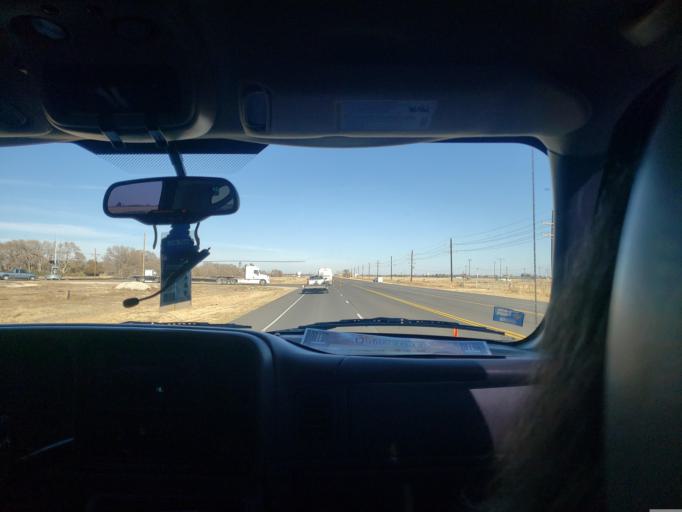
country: US
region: Texas
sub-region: Dallam County
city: Dalhart
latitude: 36.0351
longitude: -102.5636
